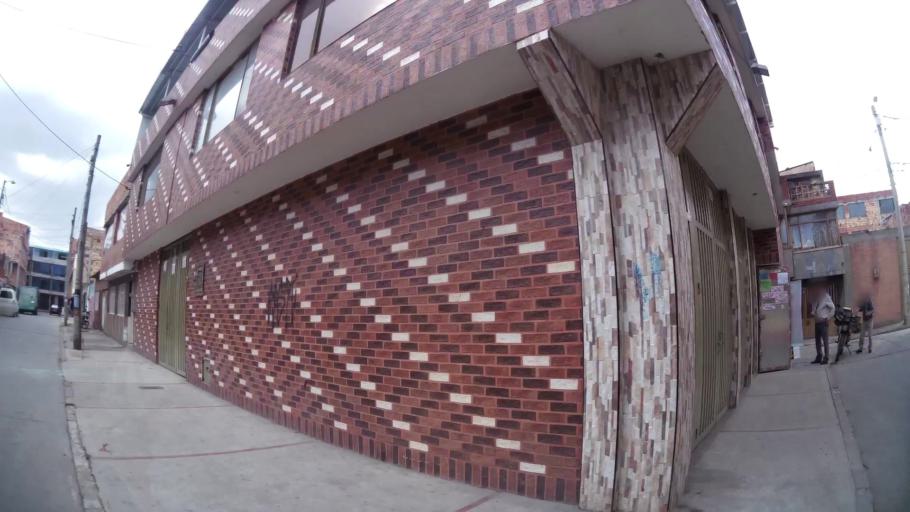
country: CO
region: Cundinamarca
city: Cota
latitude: 4.7268
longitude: -74.0955
